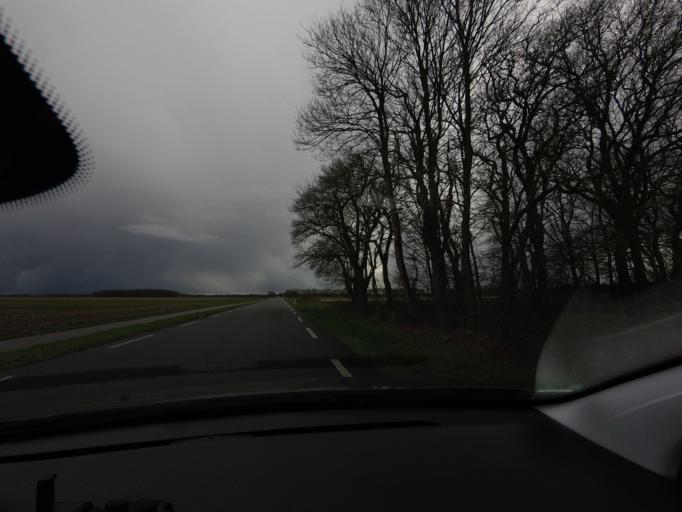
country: NL
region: Drenthe
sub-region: Gemeente Borger-Odoorn
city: Borger
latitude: 52.9448
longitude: 6.7885
